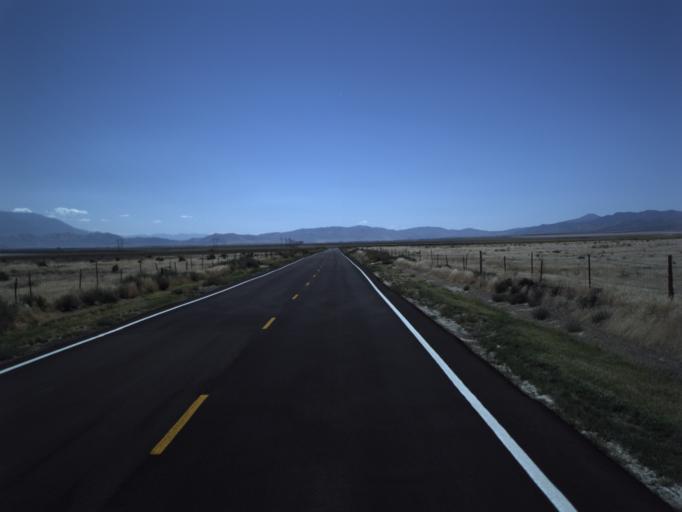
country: US
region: Utah
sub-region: Utah County
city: Eagle Mountain
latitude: 40.1493
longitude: -111.9496
